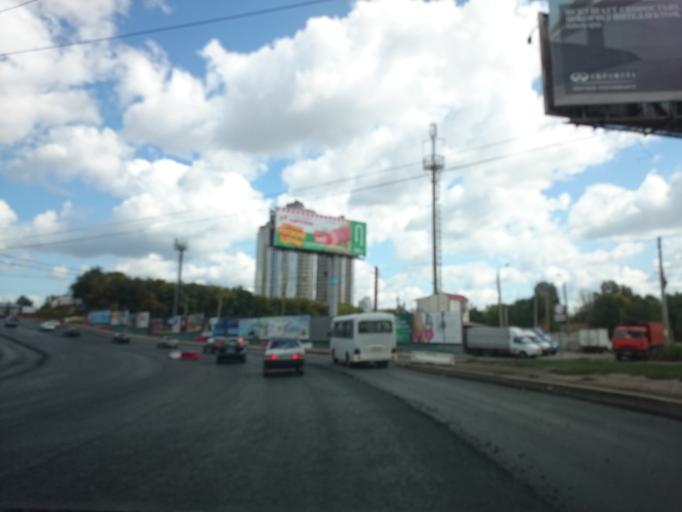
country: RU
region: Samara
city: Samara
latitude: 53.2198
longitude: 50.1637
